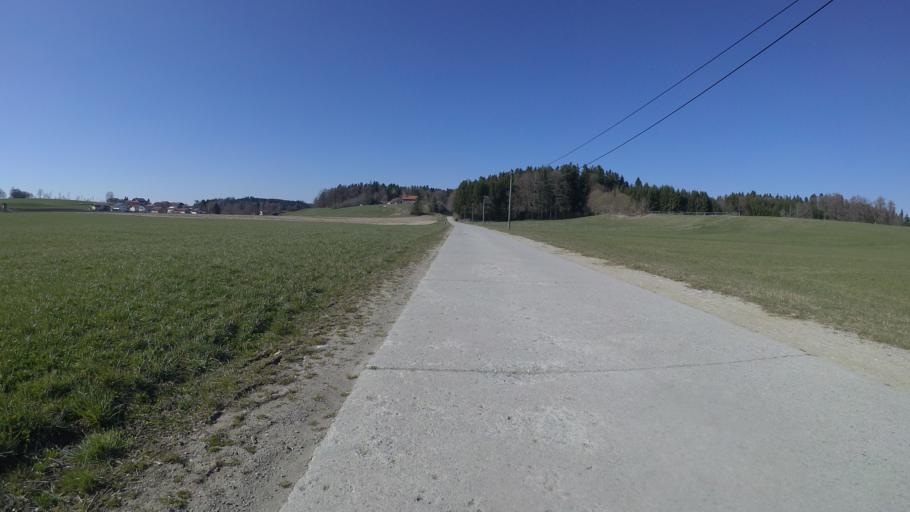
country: DE
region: Bavaria
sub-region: Upper Bavaria
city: Seeon-Seebruck
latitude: 47.9566
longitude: 12.5145
